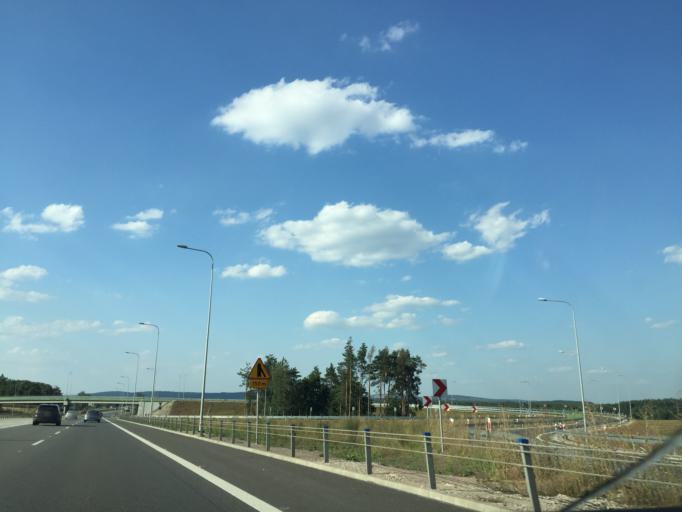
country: PL
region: Swietokrzyskie
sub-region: Powiat jedrzejowski
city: Sobkow
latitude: 50.7283
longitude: 20.4088
